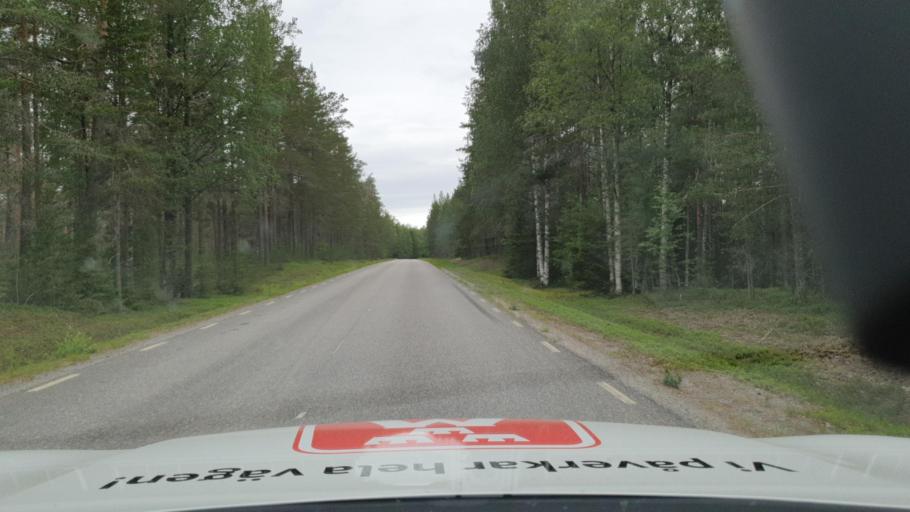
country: SE
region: Vaesterbotten
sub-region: Nordmalings Kommun
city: Nordmaling
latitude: 63.7019
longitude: 19.6177
